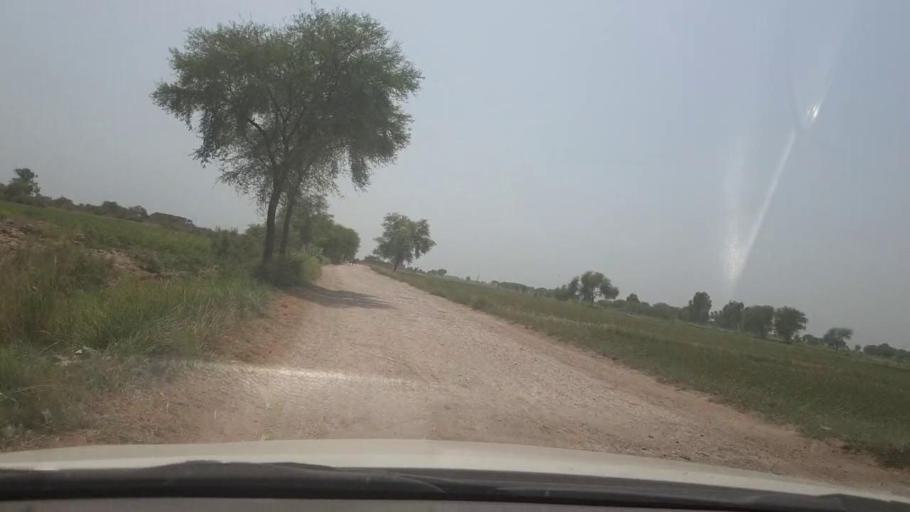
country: PK
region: Sindh
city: Shikarpur
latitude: 27.9965
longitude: 68.5874
